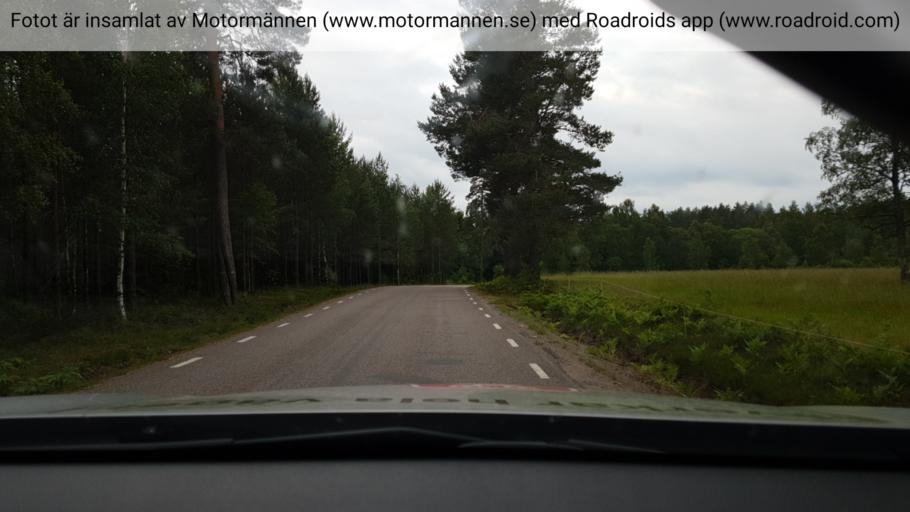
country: SE
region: Joenkoeping
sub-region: Habo Kommun
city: Habo
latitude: 58.0307
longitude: 14.0177
